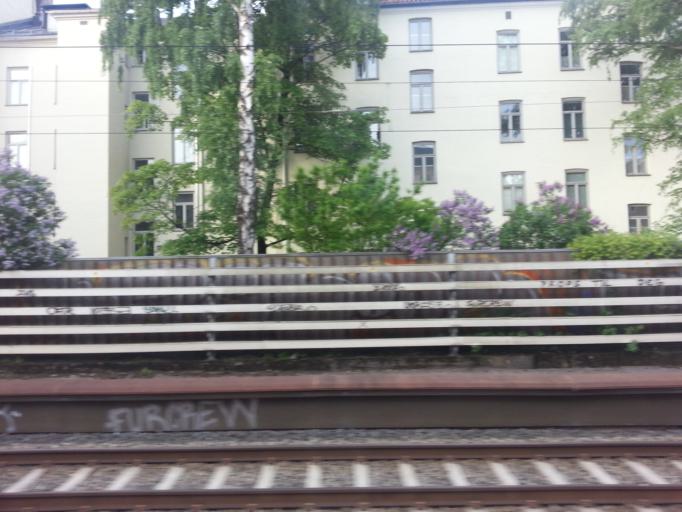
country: NO
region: Oslo
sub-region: Oslo
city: Oslo
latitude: 59.9074
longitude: 10.7717
